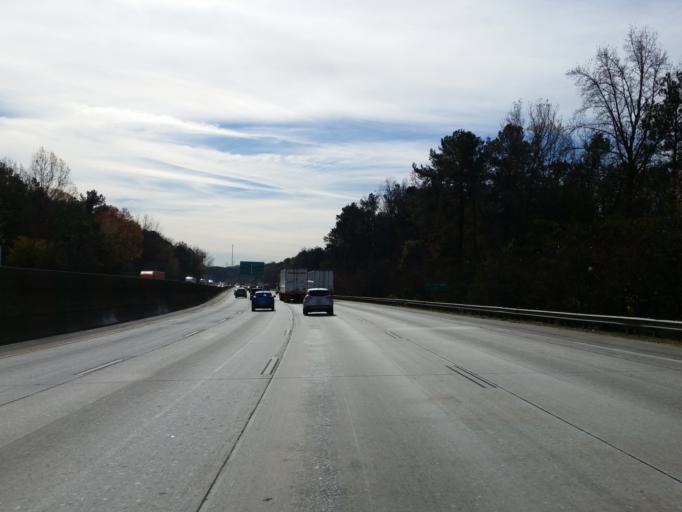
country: US
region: Georgia
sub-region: Cobb County
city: Vinings
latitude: 33.7816
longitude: -84.4962
